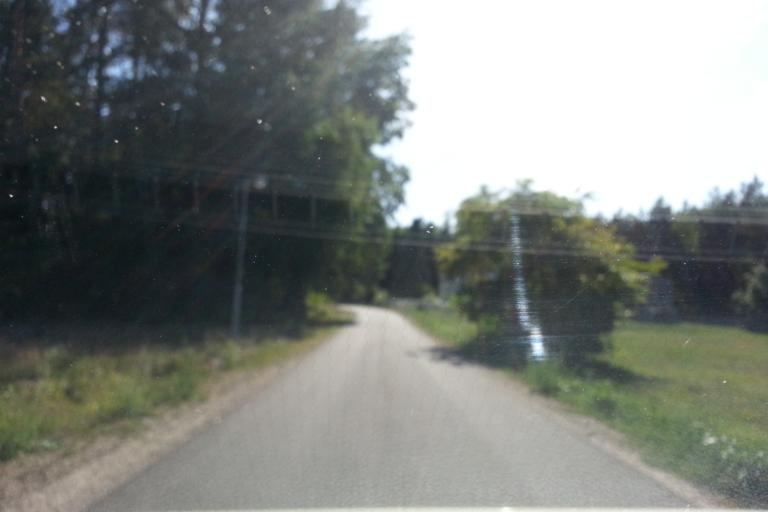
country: DE
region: Mecklenburg-Vorpommern
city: Torgelow
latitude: 53.6695
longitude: 14.0376
